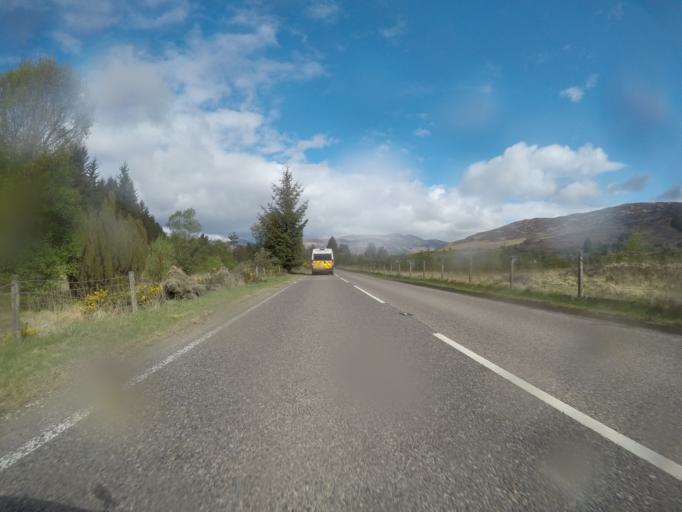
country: GB
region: Scotland
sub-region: Highland
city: Spean Bridge
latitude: 56.9097
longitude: -4.9450
